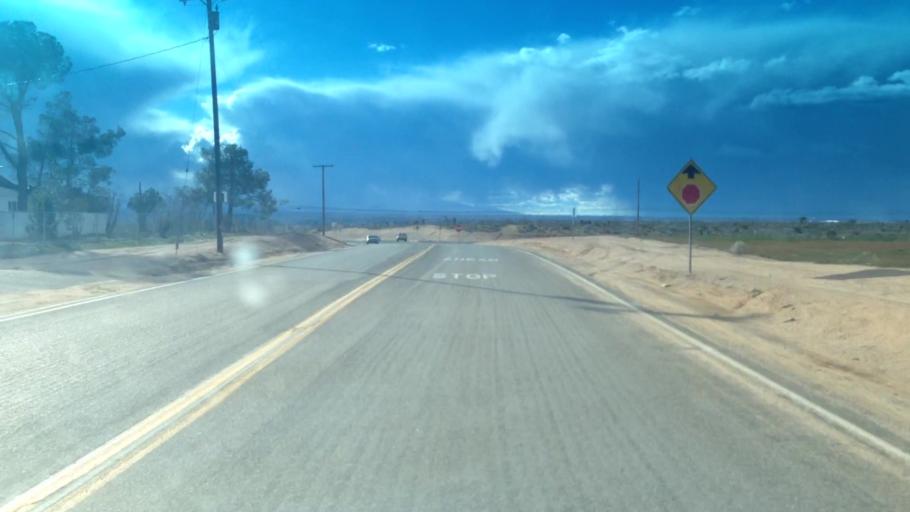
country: US
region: California
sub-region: San Bernardino County
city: Apple Valley
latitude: 34.4208
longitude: -117.2054
